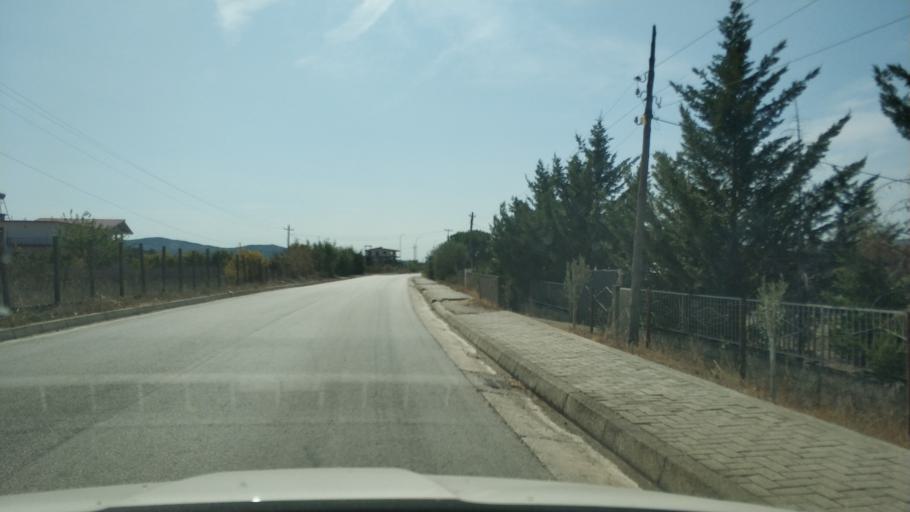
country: AL
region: Fier
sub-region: Rrethi i Lushnjes
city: Divjake
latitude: 40.9871
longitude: 19.5345
